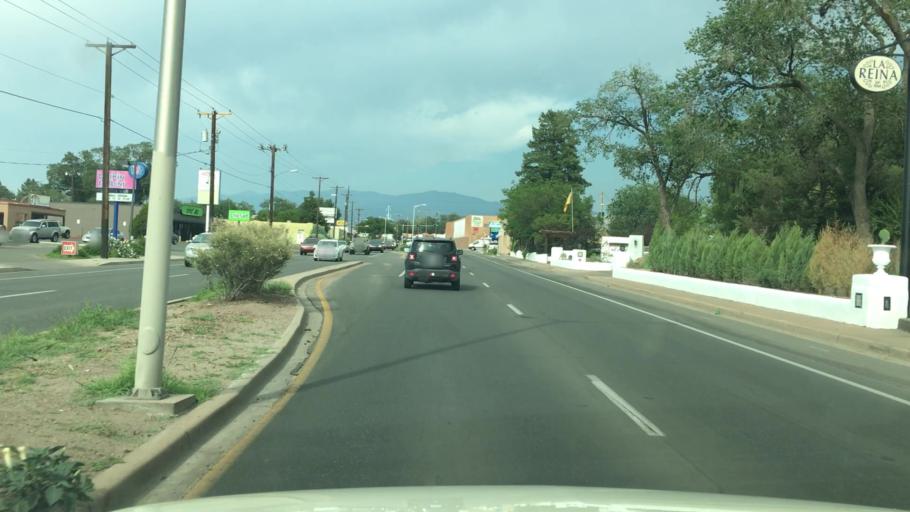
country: US
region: New Mexico
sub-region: Santa Fe County
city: Santa Fe
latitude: 35.6643
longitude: -105.9739
